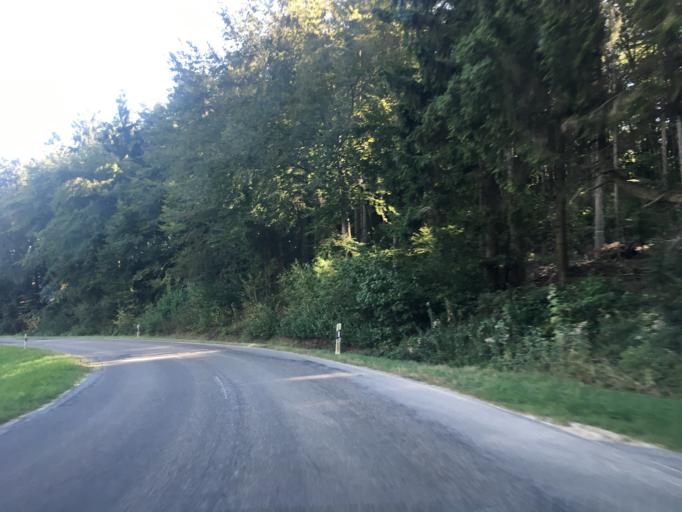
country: DE
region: Baden-Wuerttemberg
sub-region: Tuebingen Region
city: Hayingen
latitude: 48.2602
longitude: 9.5021
